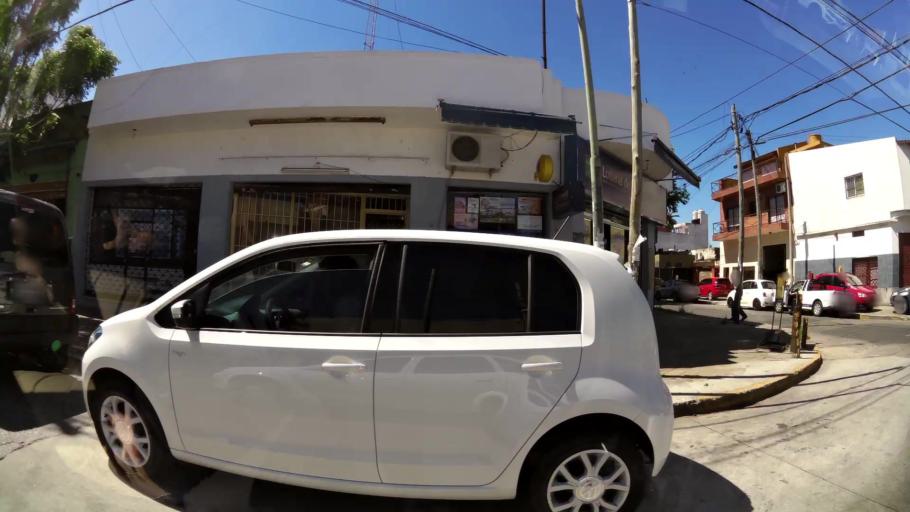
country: AR
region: Buenos Aires
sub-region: Partido de General San Martin
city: General San Martin
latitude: -34.5861
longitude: -58.5369
